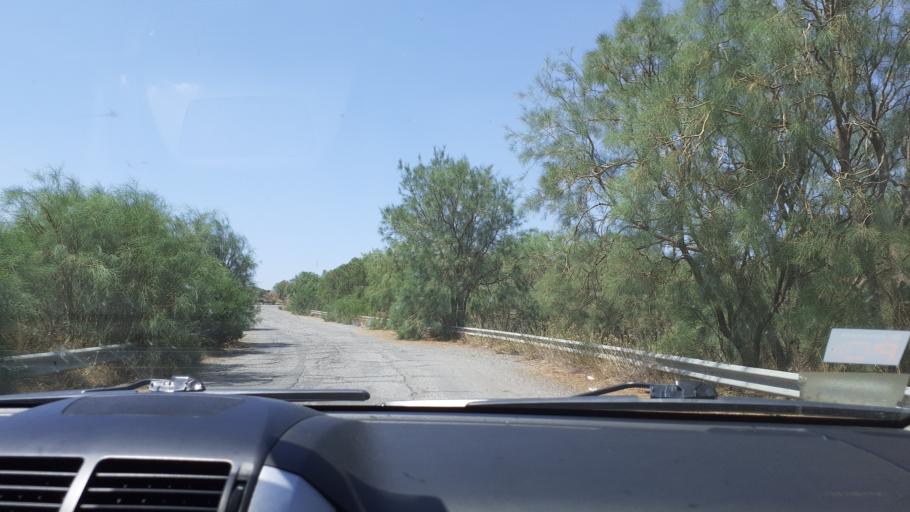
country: IT
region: Sicily
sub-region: Catania
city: Nicolosi
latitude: 37.6459
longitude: 15.0021
